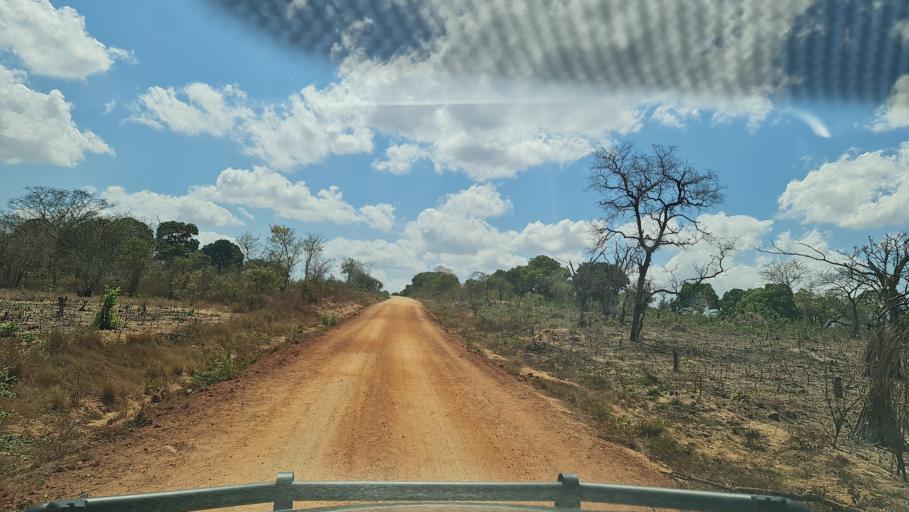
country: MZ
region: Nampula
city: Nacala
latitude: -14.1751
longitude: 40.2346
